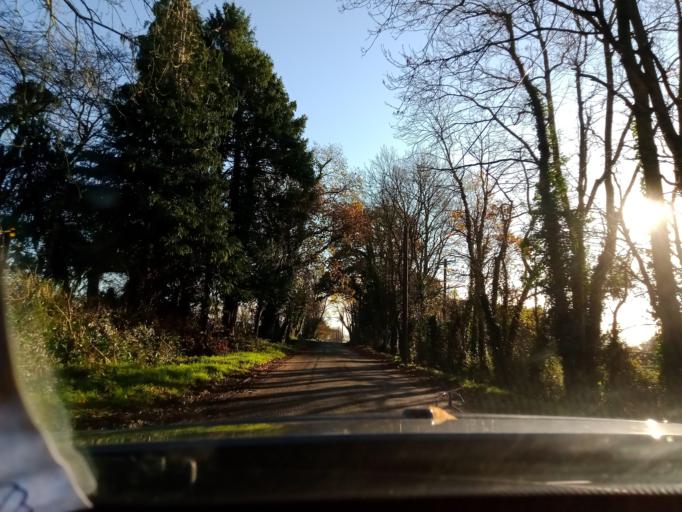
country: IE
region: Leinster
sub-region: Kilkenny
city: Mooncoin
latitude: 52.3448
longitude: -7.2756
